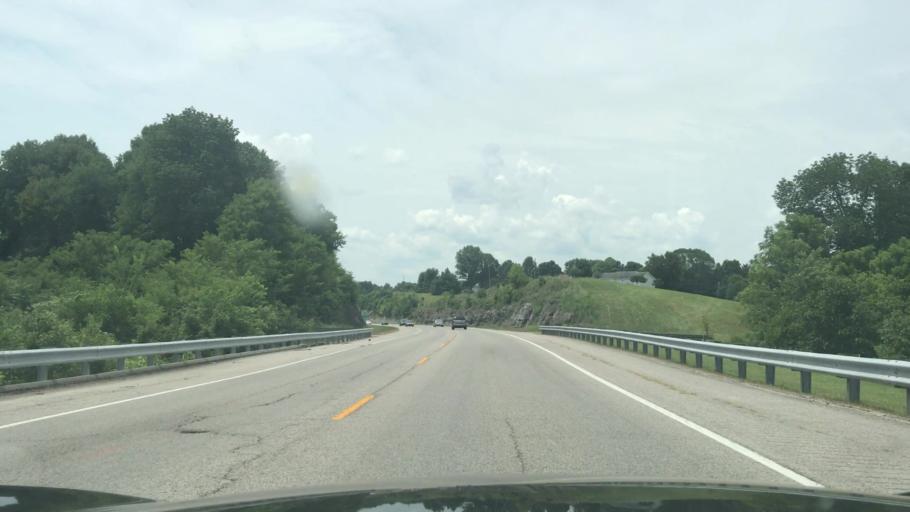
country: US
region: Kentucky
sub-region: Green County
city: Greensburg
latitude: 37.2826
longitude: -85.4876
